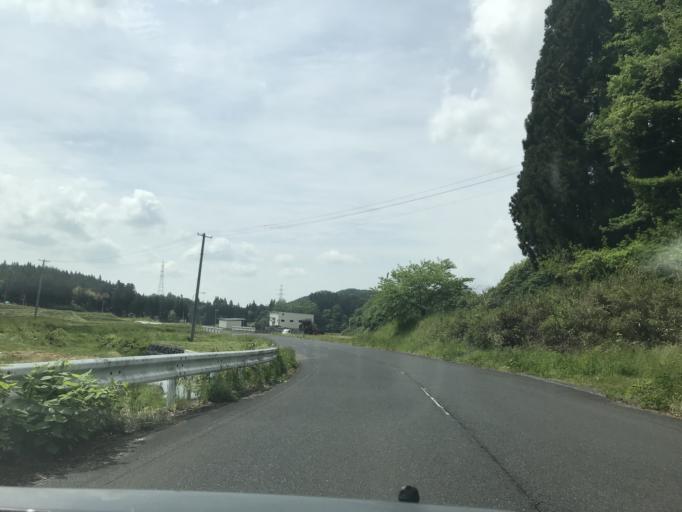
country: JP
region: Iwate
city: Ichinoseki
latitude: 38.8715
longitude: 140.9797
